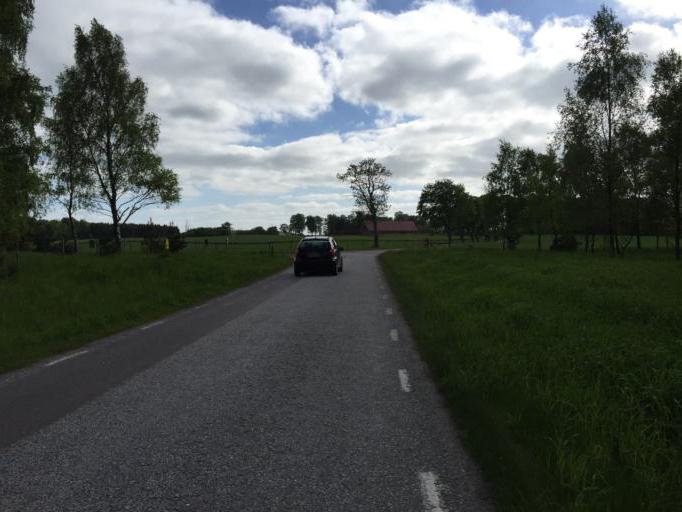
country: SE
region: Skane
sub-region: Sjobo Kommun
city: Blentarp
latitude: 55.6530
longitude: 13.6046
